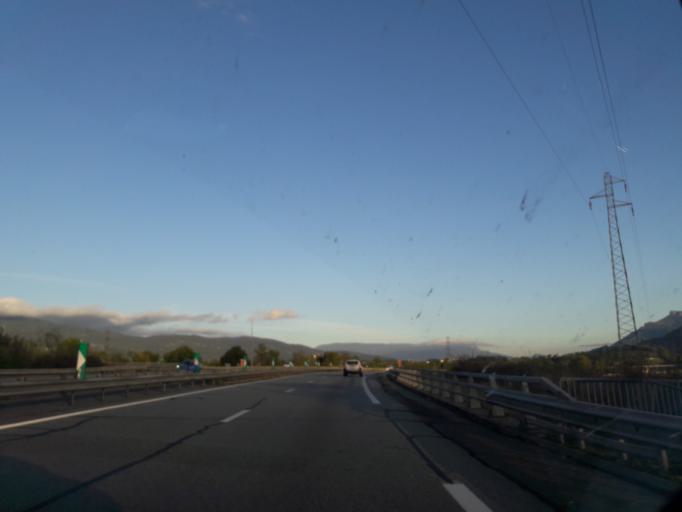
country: FR
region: Rhone-Alpes
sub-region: Departement de la Savoie
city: Montmelian
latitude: 45.4837
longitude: 6.0260
